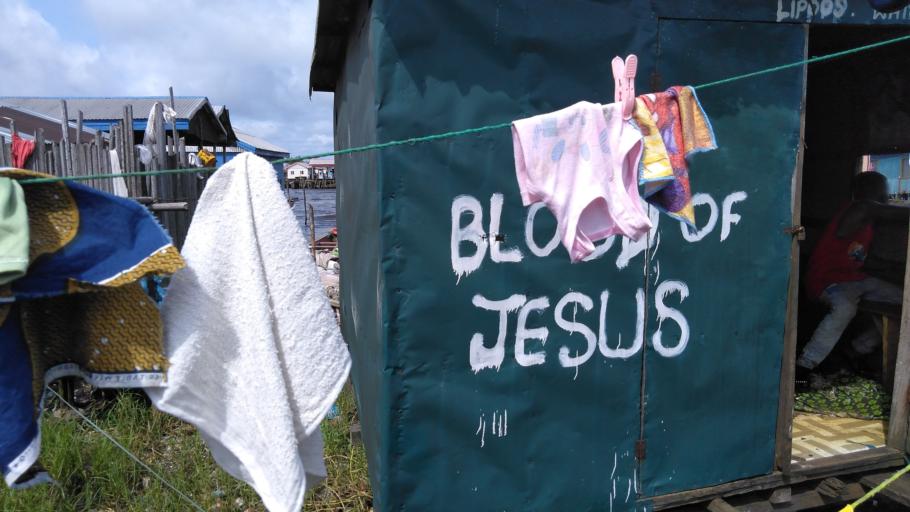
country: NG
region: Ondo
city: Igbekebo
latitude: 5.9236
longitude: 4.9651
